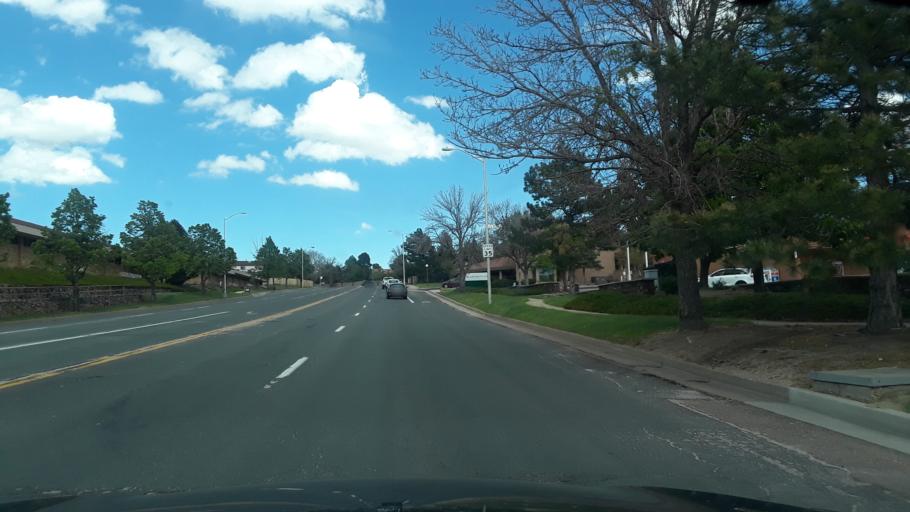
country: US
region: Colorado
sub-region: El Paso County
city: Black Forest
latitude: 38.9417
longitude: -104.7749
